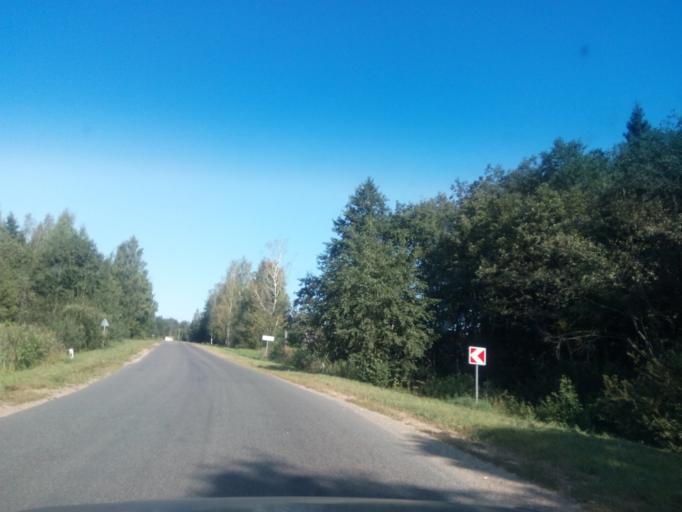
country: BY
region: Vitebsk
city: Dzisna
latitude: 55.6510
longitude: 28.3242
